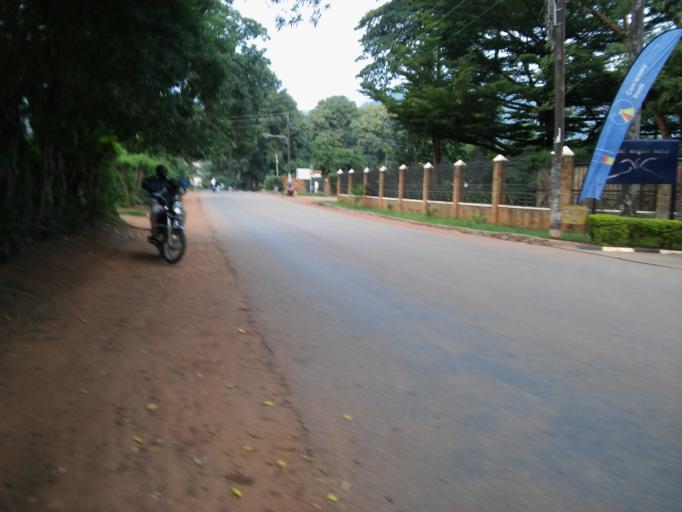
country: UG
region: Eastern Region
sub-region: Mbale District
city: Mbale
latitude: 1.0670
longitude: 34.1949
